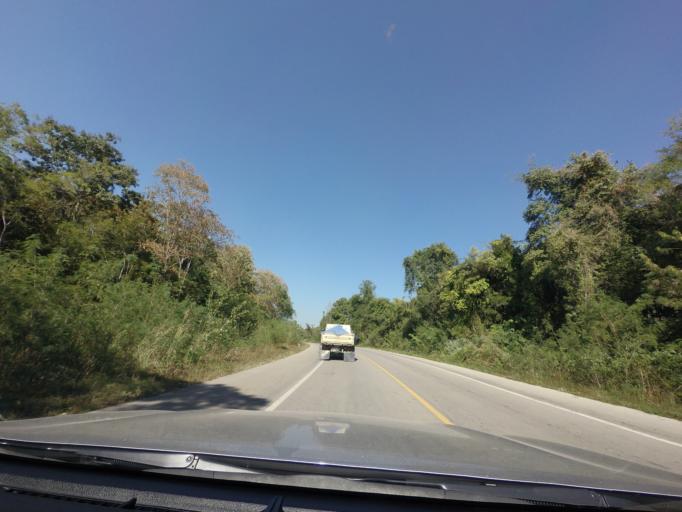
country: TH
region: Lampang
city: Mae Mo
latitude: 18.4960
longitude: 99.6469
